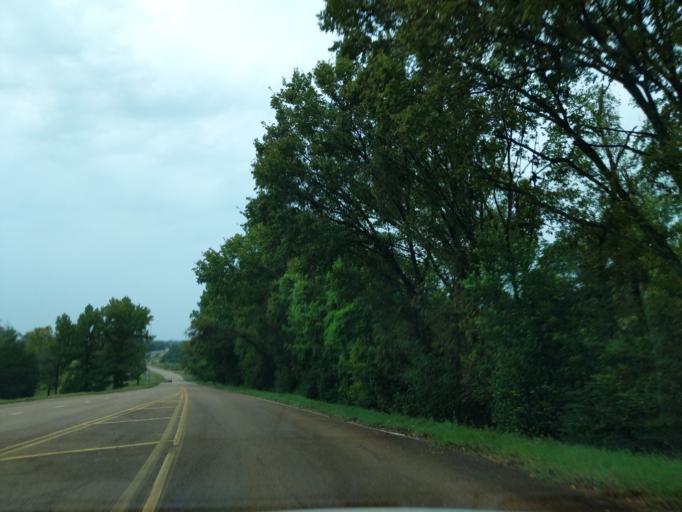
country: US
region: Mississippi
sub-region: Warren County
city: Vicksburg
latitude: 32.3218
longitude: -90.8776
